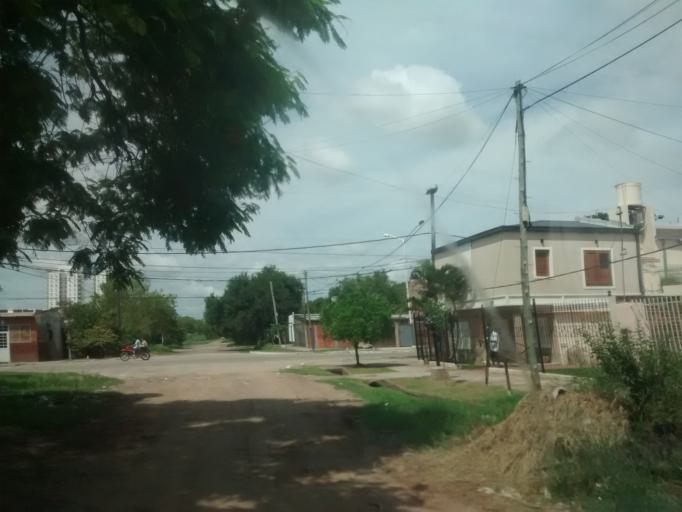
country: AR
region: Chaco
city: Resistencia
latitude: -27.4366
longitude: -58.9880
